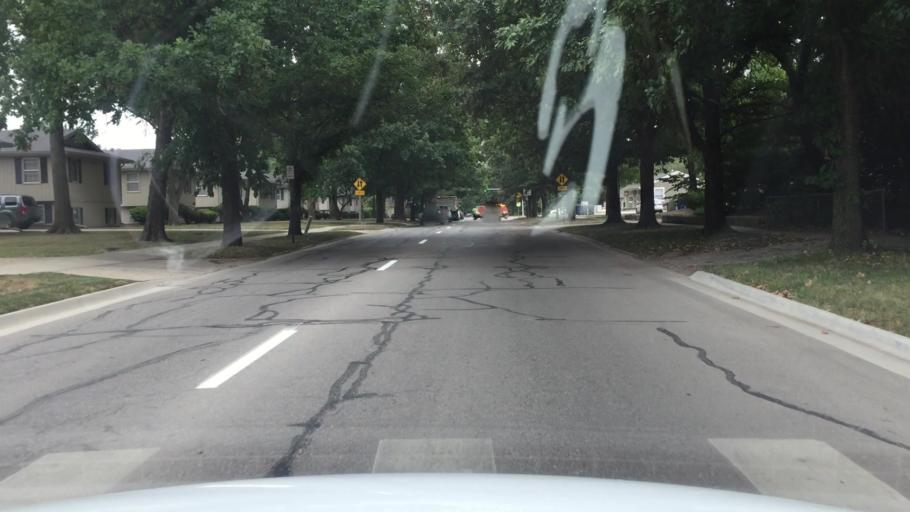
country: US
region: Kansas
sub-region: Douglas County
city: Lawrence
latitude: 38.9518
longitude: -95.2394
